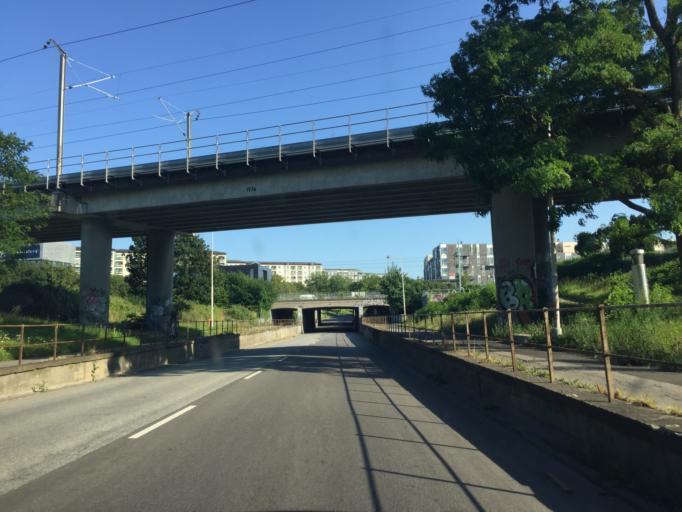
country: DK
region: Capital Region
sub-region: Frederiksberg Kommune
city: Frederiksberg
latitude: 55.7121
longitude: 12.5520
